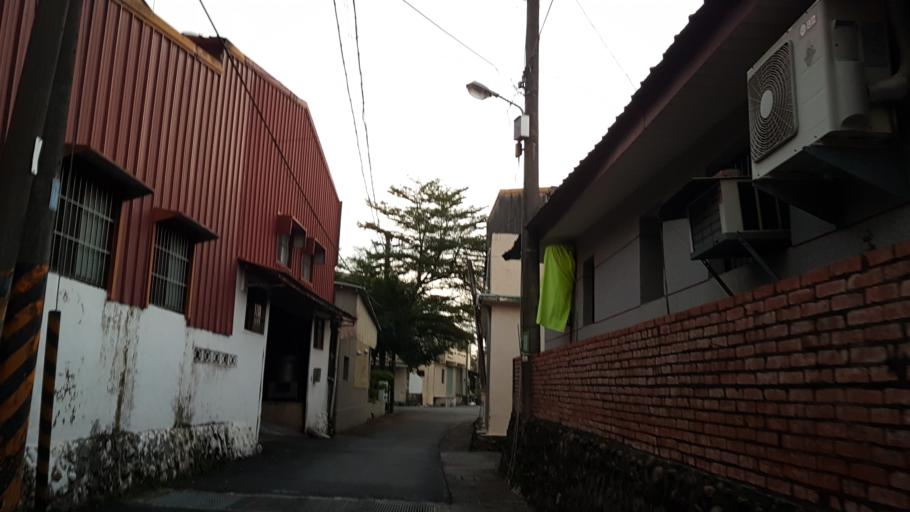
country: TW
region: Taiwan
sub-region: Chiayi
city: Jiayi Shi
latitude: 23.3666
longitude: 120.4624
